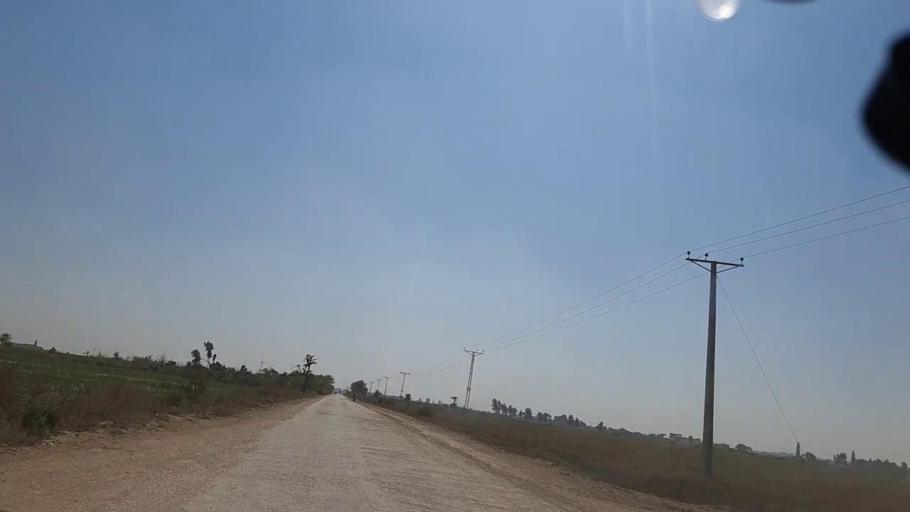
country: PK
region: Sindh
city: Mirpur Khas
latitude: 25.5005
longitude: 69.0346
